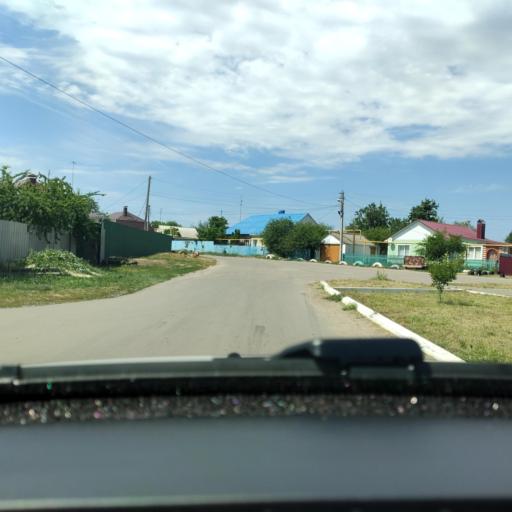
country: RU
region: Voronezj
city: Maslovka
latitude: 51.5050
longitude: 39.2968
